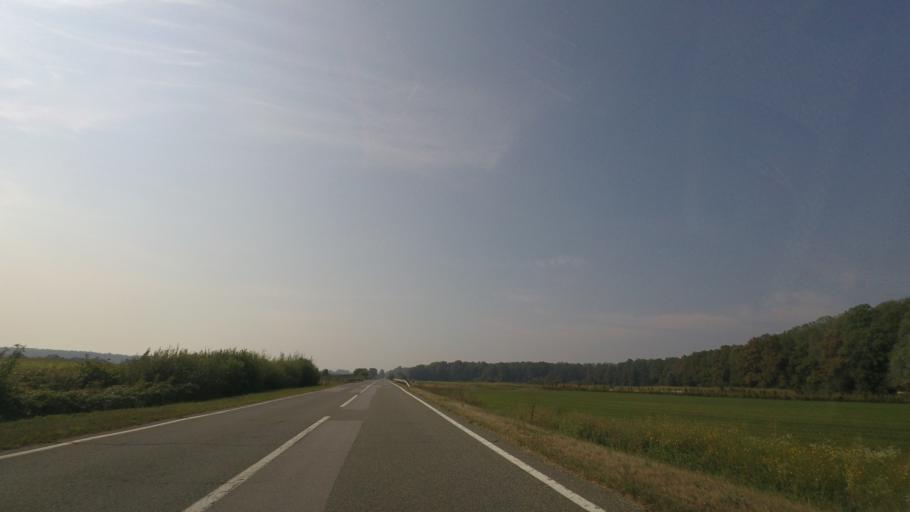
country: HR
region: Sisacko-Moslavacka
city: Novska
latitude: 45.3169
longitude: 16.9492
